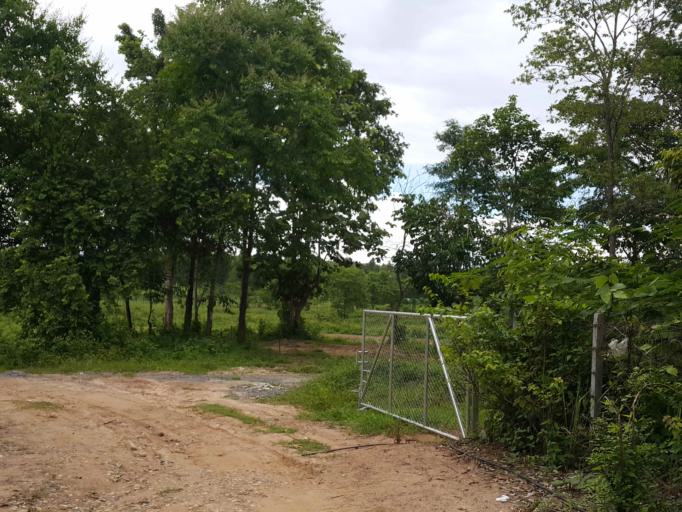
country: TH
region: Chiang Mai
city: San Sai
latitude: 18.9419
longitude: 98.9106
